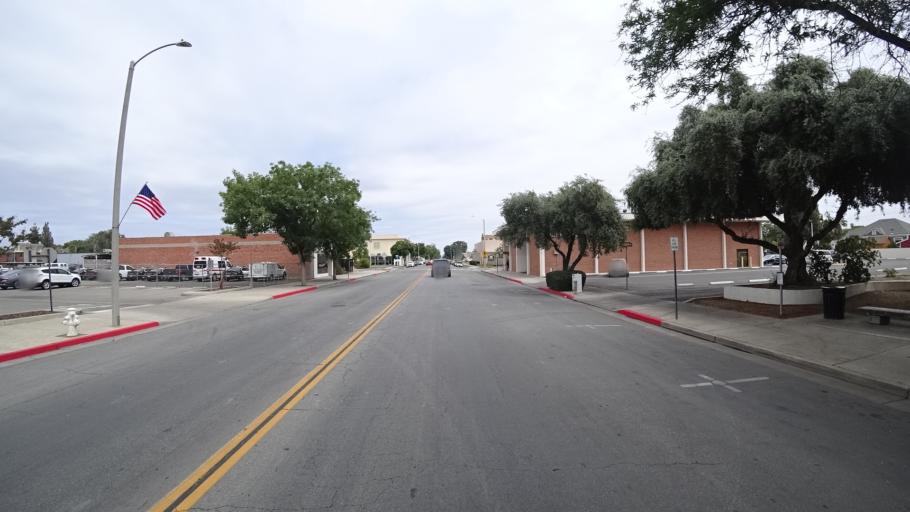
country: US
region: California
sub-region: Kings County
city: Hanford
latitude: 36.3294
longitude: -119.6460
